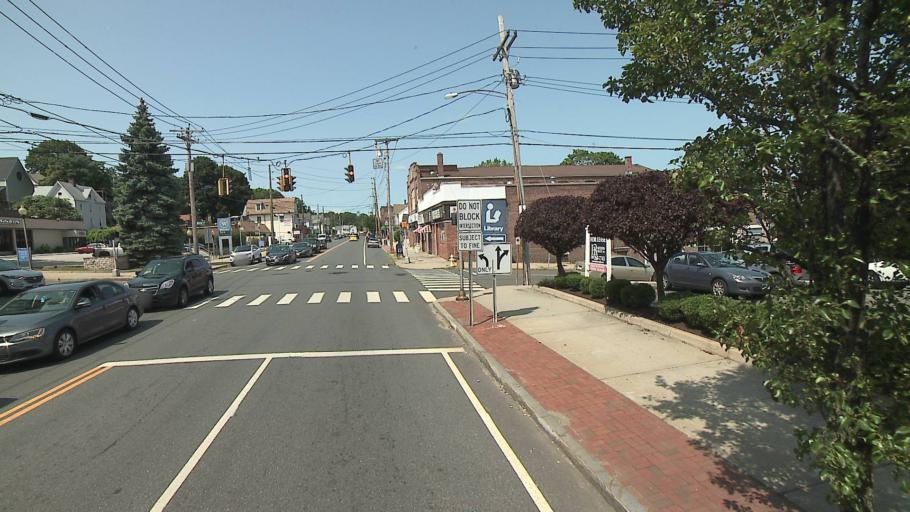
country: US
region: Connecticut
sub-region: Fairfield County
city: Shelton
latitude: 41.3180
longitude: -73.0942
